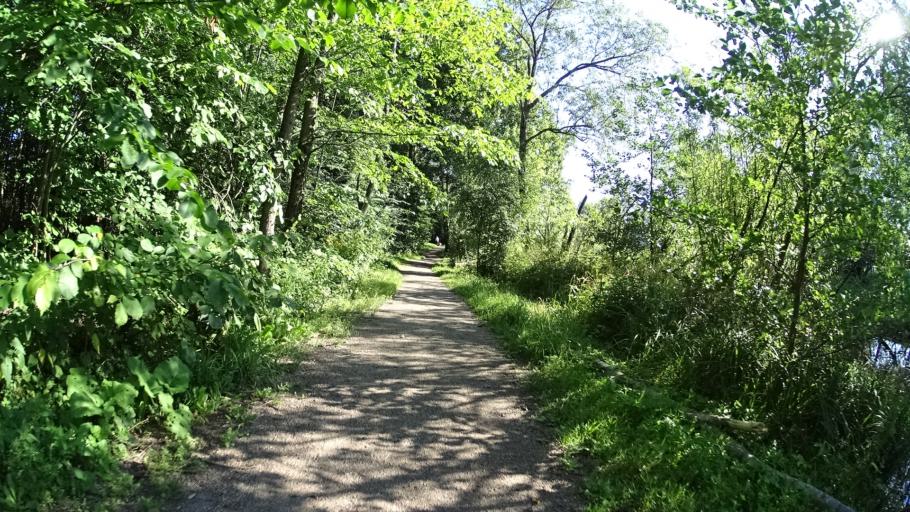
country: FI
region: Uusimaa
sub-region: Helsinki
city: Teekkarikylae
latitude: 60.2432
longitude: 24.8696
